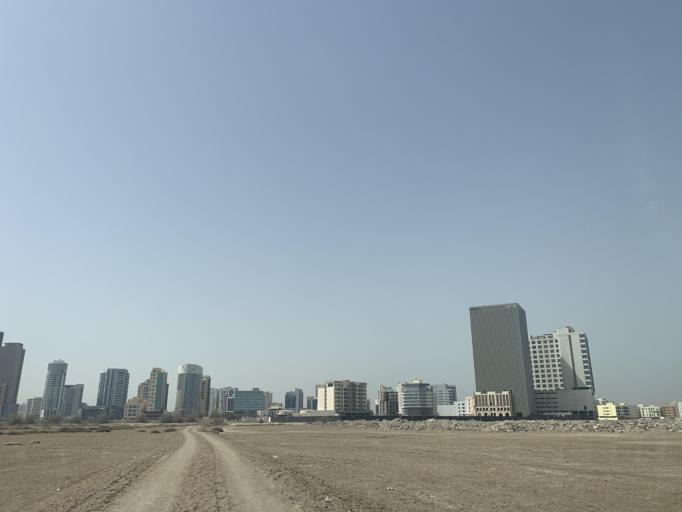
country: BH
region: Manama
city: Jidd Hafs
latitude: 26.2461
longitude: 50.5332
